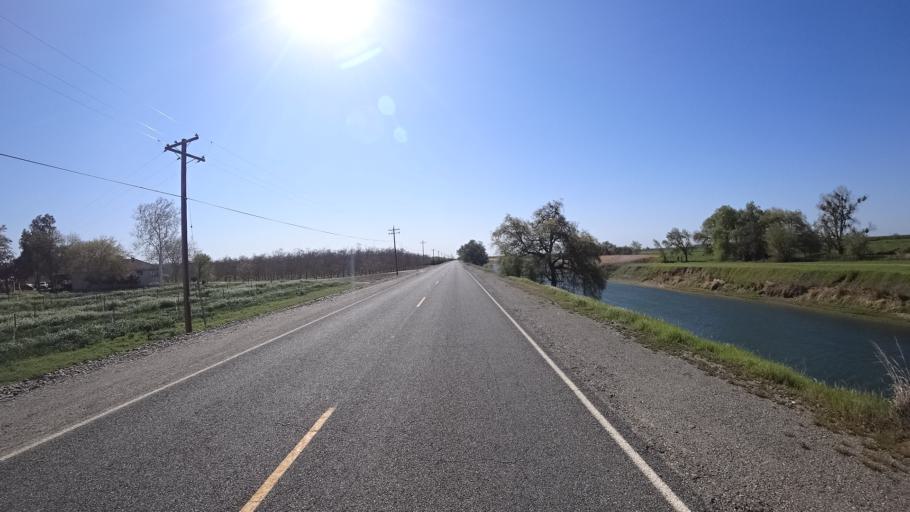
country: US
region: California
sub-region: Glenn County
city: Hamilton City
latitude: 39.7820
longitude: -122.0440
